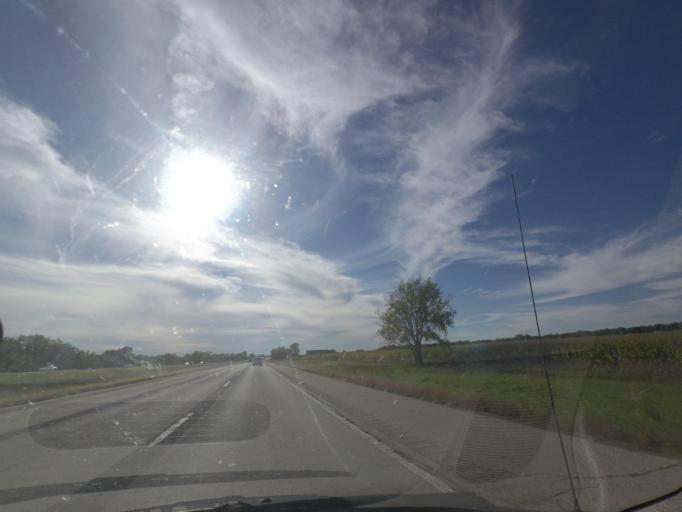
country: US
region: Illinois
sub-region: Macon County
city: Harristown
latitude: 39.8357
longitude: -89.0624
